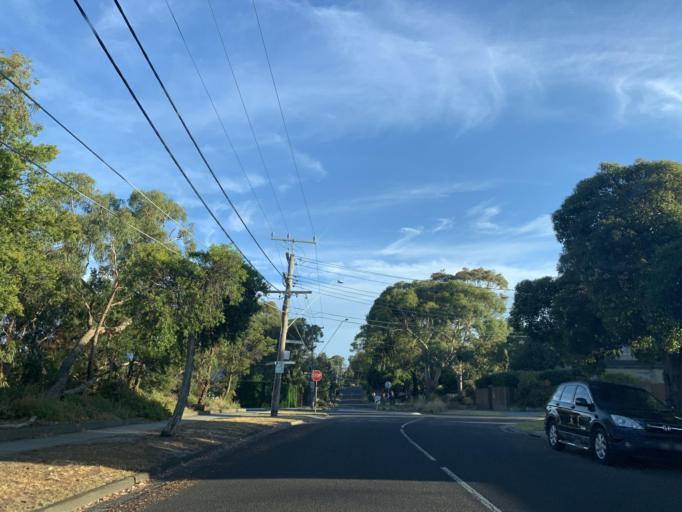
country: AU
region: Victoria
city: Beaumaris
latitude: -37.9821
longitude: 145.0290
